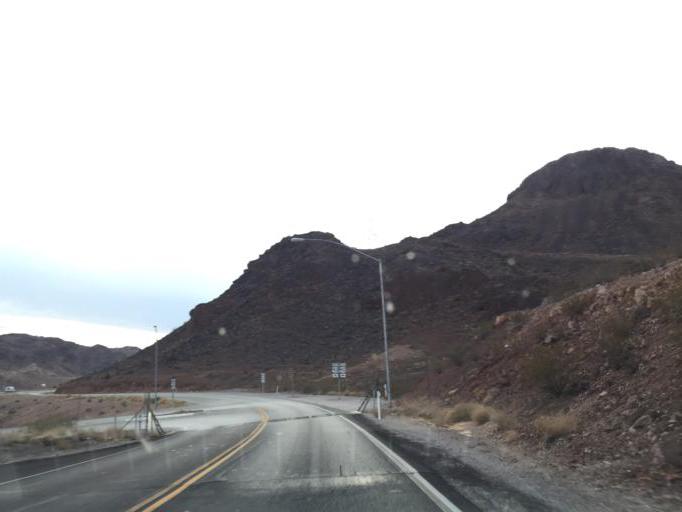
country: US
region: Nevada
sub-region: Clark County
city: Boulder City
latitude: 36.0124
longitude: -114.7741
